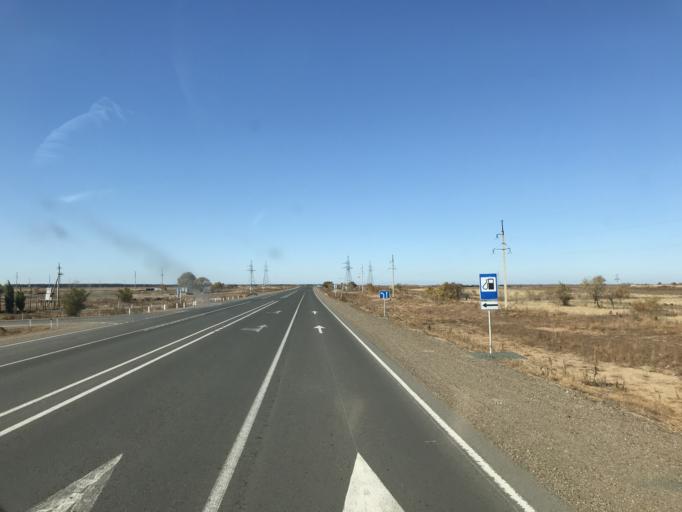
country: KZ
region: Pavlodar
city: Kurchatov
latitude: 51.0554
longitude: 79.1162
